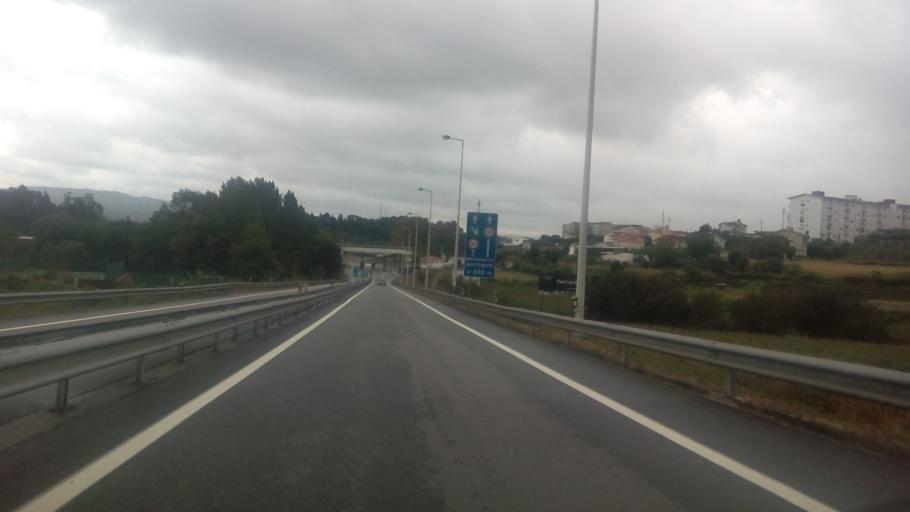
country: PT
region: Porto
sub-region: Paredes
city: Casteloes de Cepeda
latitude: 41.2046
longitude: -8.3365
